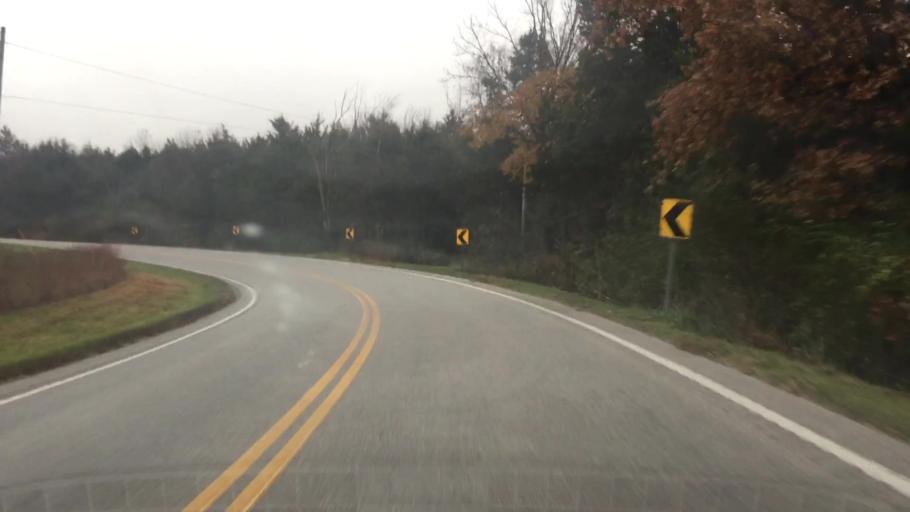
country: US
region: Missouri
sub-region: Callaway County
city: Fulton
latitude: 38.8763
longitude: -92.0790
